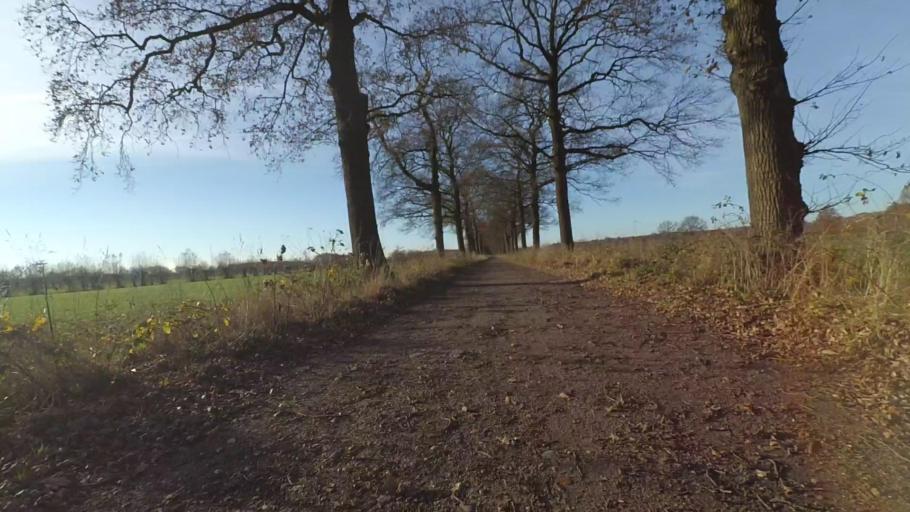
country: NL
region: Utrecht
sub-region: Gemeente Utrechtse Heuvelrug
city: Doorn
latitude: 52.0157
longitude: 5.3646
